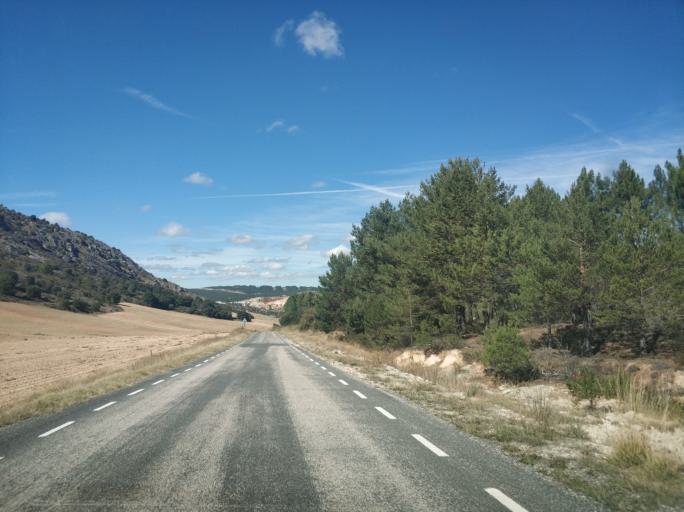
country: ES
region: Castille and Leon
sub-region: Provincia de Soria
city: Espejon
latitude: 41.8221
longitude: -3.2439
